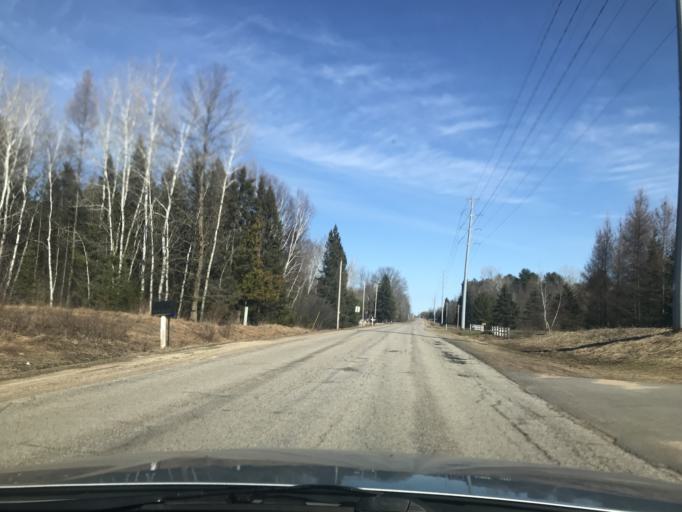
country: US
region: Wisconsin
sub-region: Marinette County
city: Marinette
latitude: 45.1449
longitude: -87.6471
